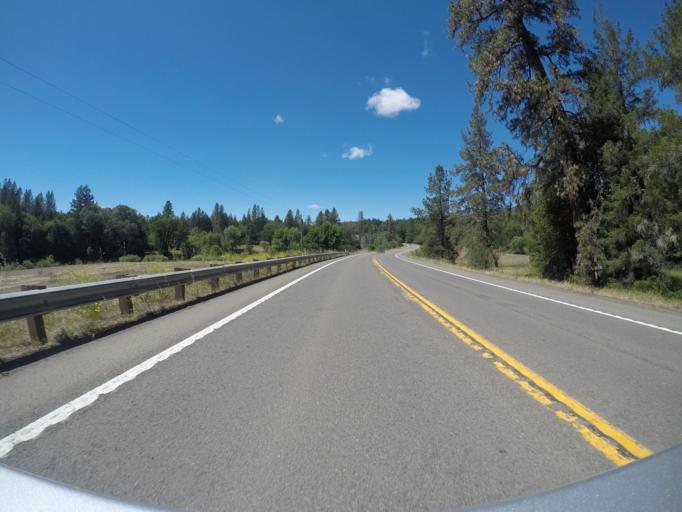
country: US
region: California
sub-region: Mendocino County
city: Laytonville
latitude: 39.7351
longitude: -123.5135
